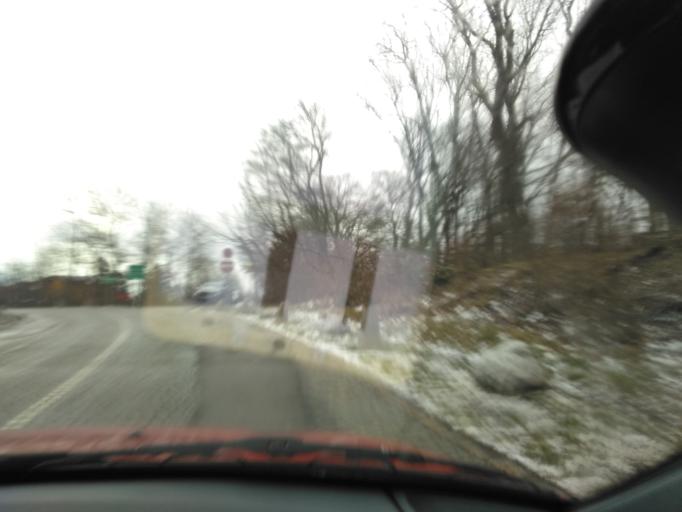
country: AT
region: Lower Austria
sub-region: Politischer Bezirk Wien-Umgebung
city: Klosterneuburg
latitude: 48.2637
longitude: 16.3128
